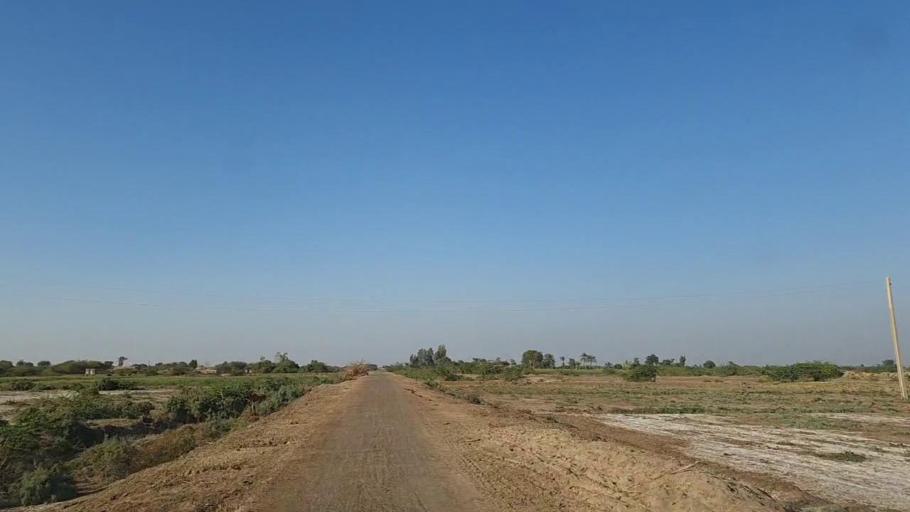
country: PK
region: Sindh
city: Samaro
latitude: 25.3462
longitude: 69.3674
